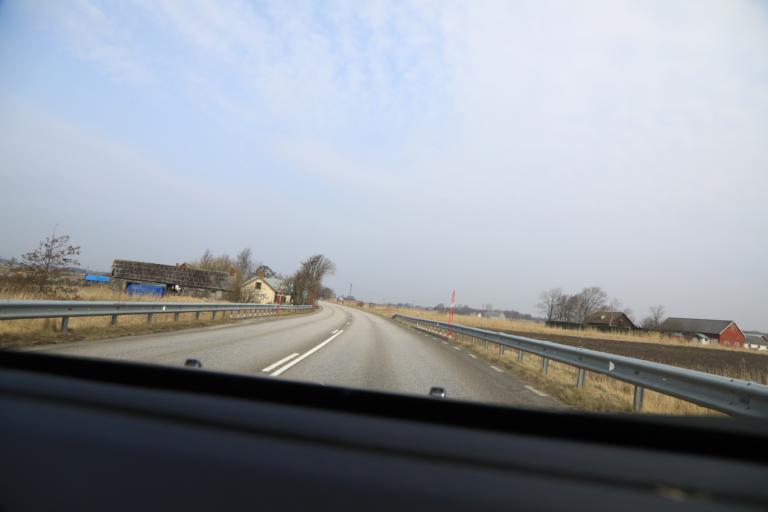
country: SE
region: Halland
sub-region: Kungsbacka Kommun
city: Frillesas
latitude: 57.2591
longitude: 12.1807
